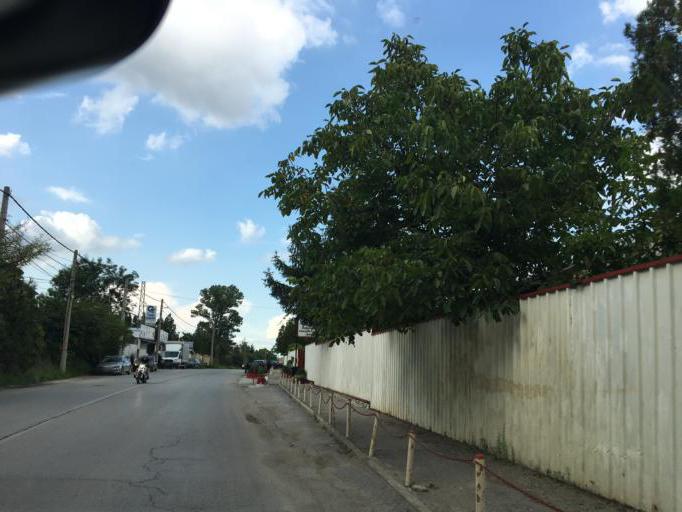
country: BG
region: Sofia-Capital
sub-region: Stolichna Obshtina
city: Sofia
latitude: 42.6406
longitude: 23.3532
